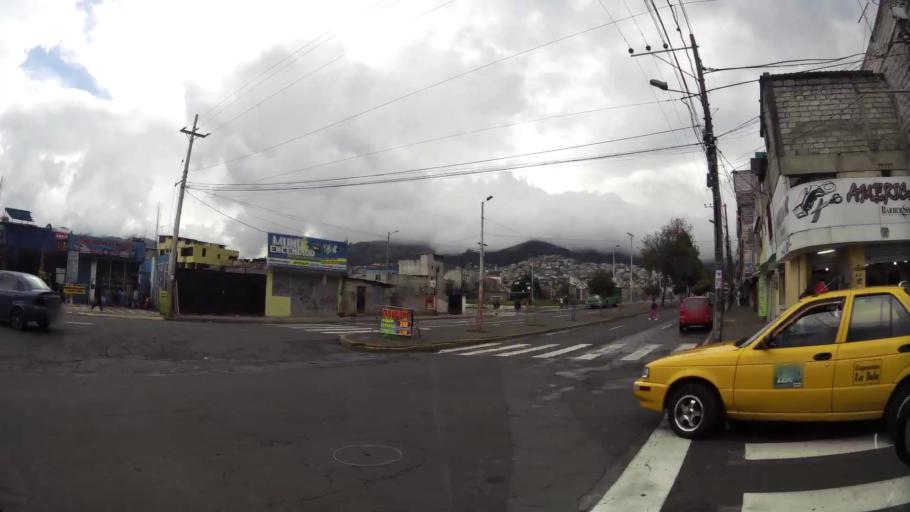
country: EC
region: Pichincha
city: Quito
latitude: -0.2701
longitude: -78.5446
